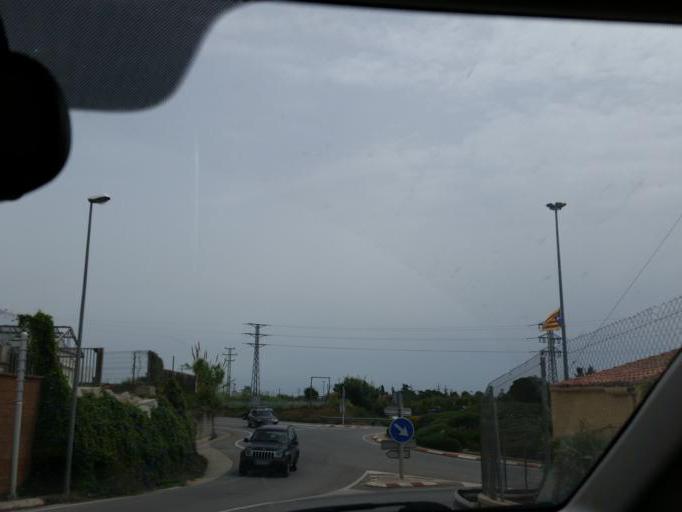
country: ES
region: Catalonia
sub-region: Provincia de Barcelona
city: Cabrera de Mar
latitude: 41.5176
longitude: 2.3969
